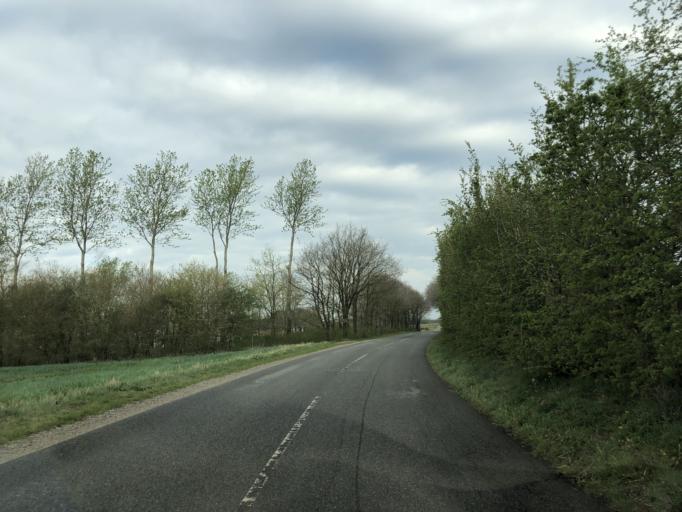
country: DK
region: Central Jutland
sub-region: Holstebro Kommune
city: Holstebro
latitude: 56.3240
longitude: 8.5043
